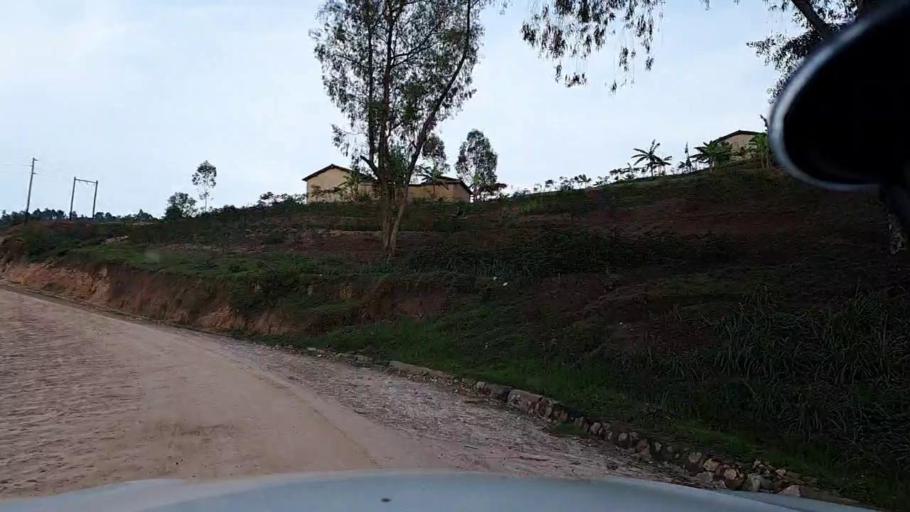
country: RW
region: Southern Province
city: Nyanza
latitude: -2.2266
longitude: 29.6537
